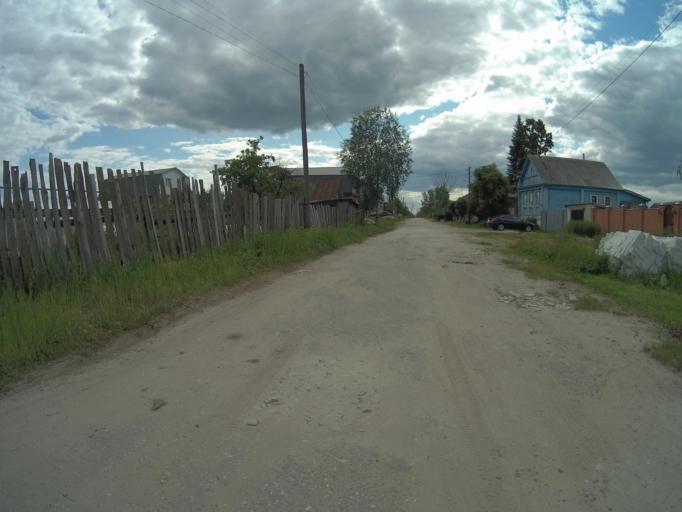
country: RU
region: Vladimir
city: Sudogda
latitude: 55.9559
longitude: 40.8668
